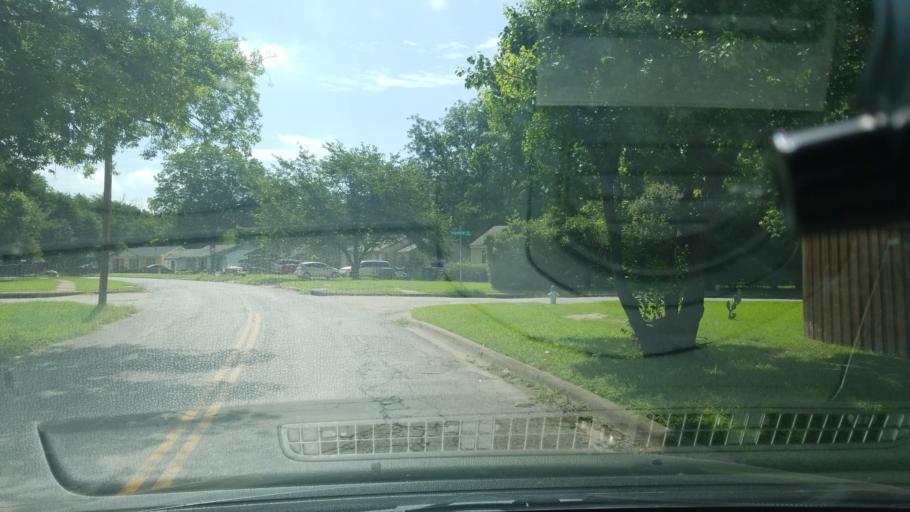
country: US
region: Texas
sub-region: Dallas County
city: Balch Springs
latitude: 32.7373
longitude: -96.6923
